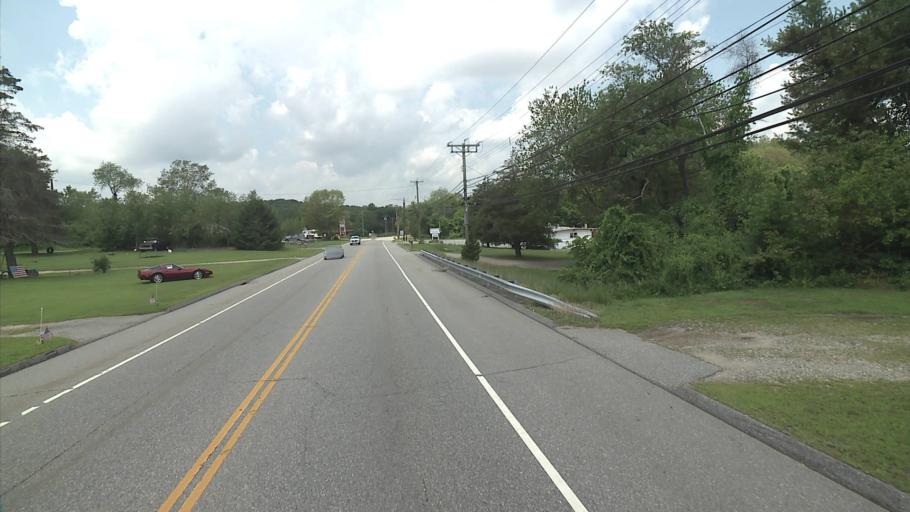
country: US
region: Connecticut
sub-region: New London County
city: Jewett City
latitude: 41.5879
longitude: -71.9514
